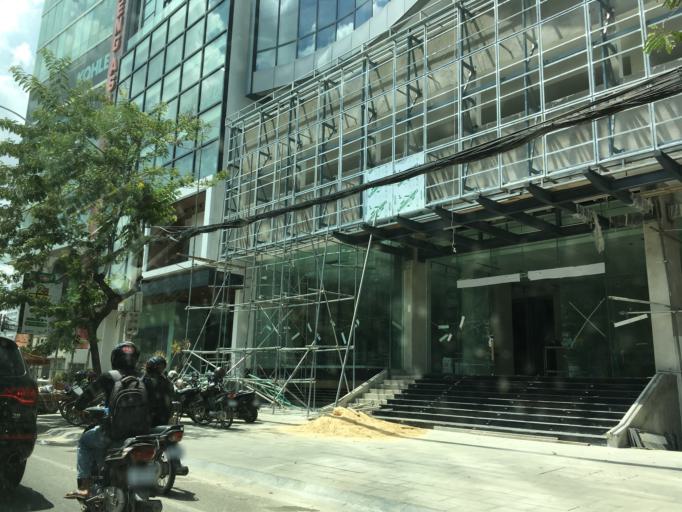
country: KH
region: Phnom Penh
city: Phnom Penh
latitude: 11.5440
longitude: 104.9210
